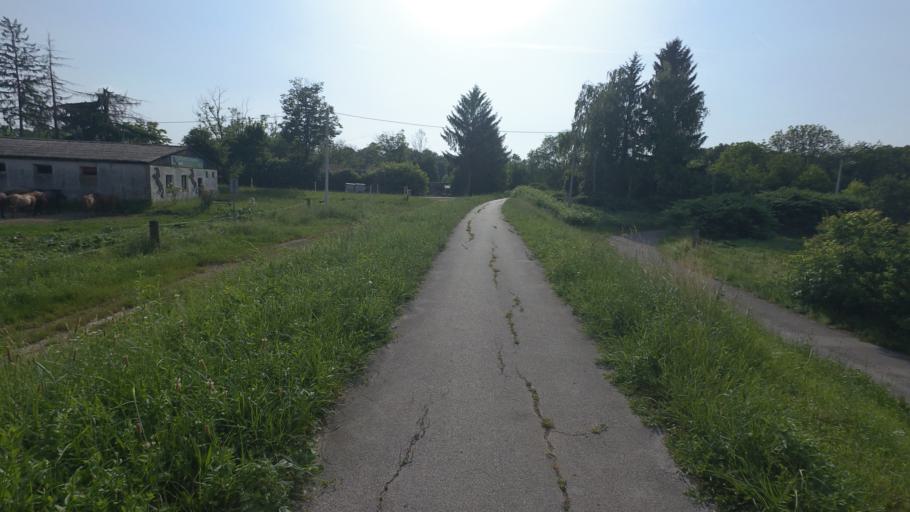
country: HR
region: Karlovacka
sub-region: Grad Karlovac
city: Karlovac
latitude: 45.4902
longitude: 15.5672
